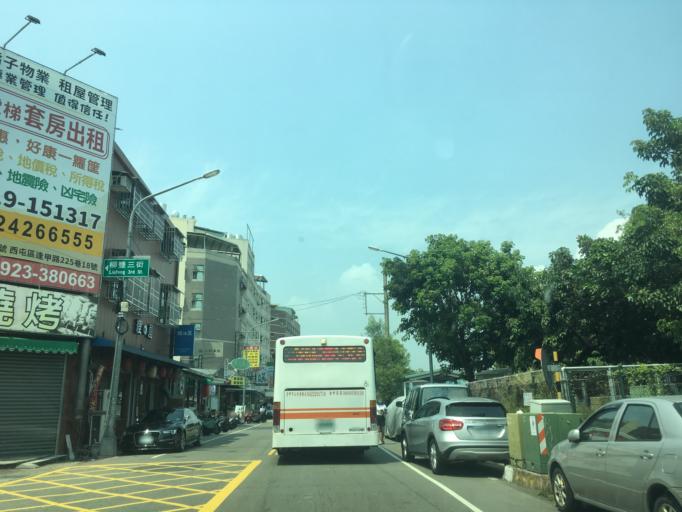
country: TW
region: Taiwan
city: Zhongxing New Village
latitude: 24.0438
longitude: 120.6887
